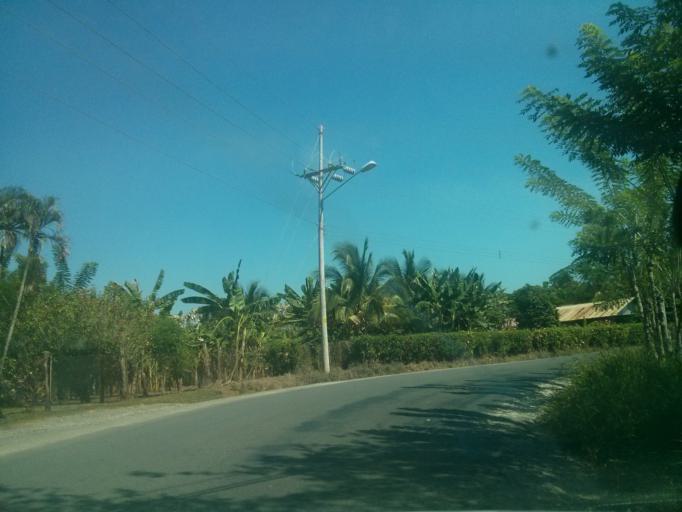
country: CR
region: Puntarenas
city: Paquera
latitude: 9.6575
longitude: -85.1230
